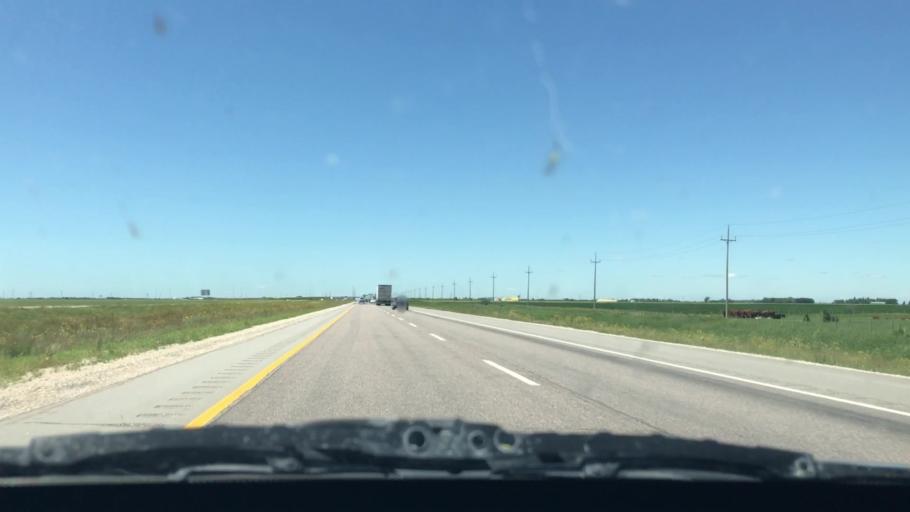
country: CA
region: Manitoba
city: Steinbach
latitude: 49.6909
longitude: -96.6200
